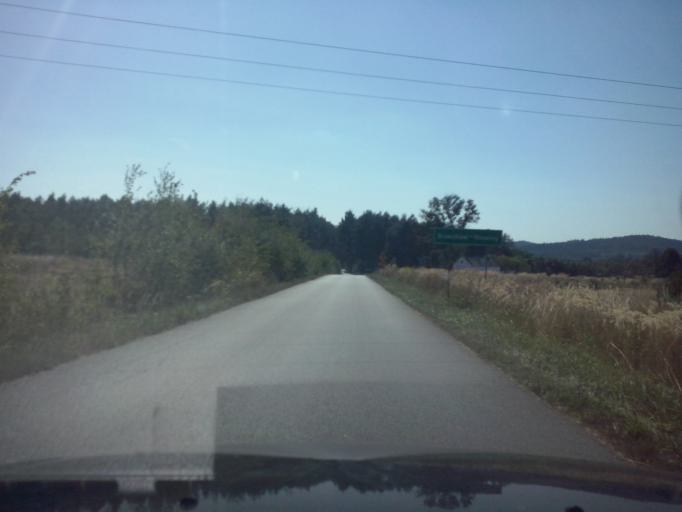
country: PL
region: Swietokrzyskie
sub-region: Powiat kielecki
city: Gorno
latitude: 50.8459
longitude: 20.7690
